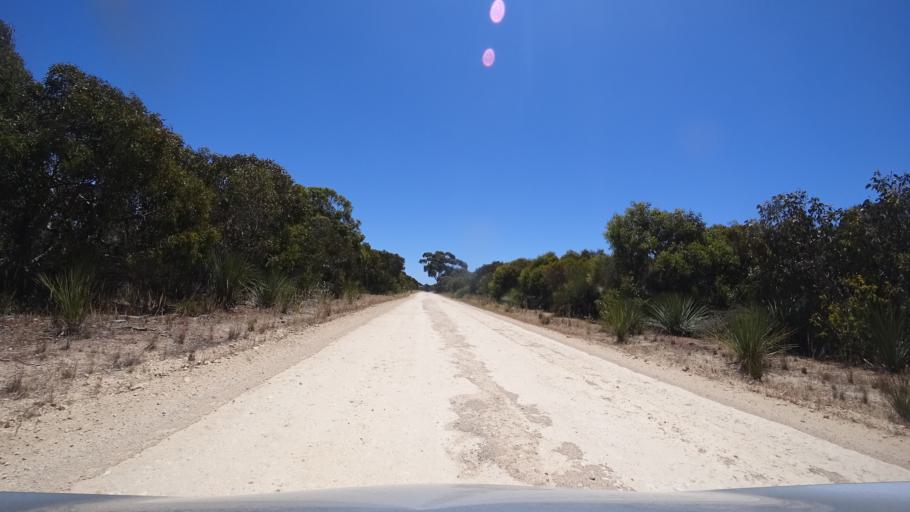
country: AU
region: South Australia
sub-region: Kangaroo Island
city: Kingscote
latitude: -35.6696
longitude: 137.1101
